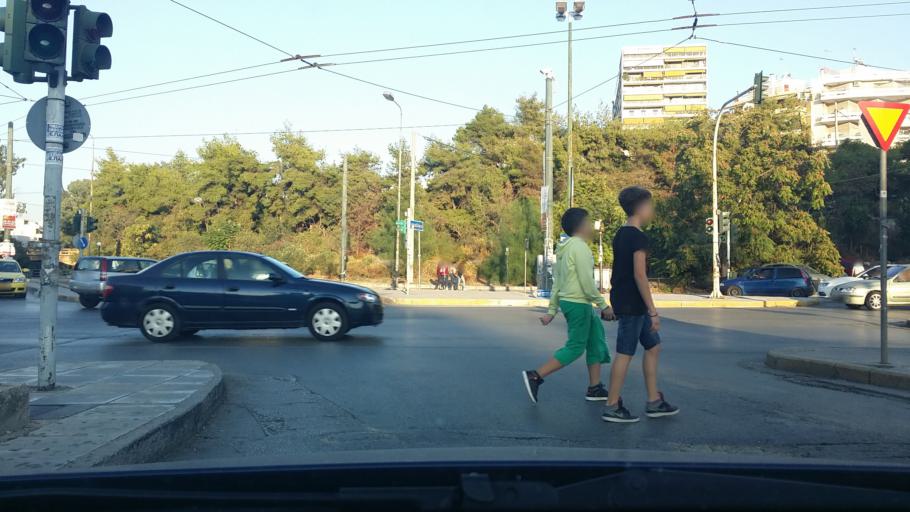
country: GR
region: Attica
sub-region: Nomarchia Athinas
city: Nea Chalkidona
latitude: 38.0259
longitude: 23.7311
